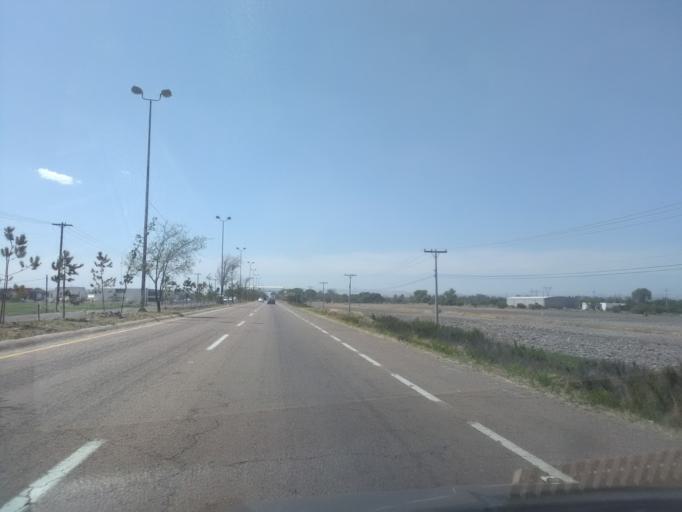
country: MX
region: Durango
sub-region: Durango
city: Jose Refugio Salcido
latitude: 24.0237
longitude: -104.5486
